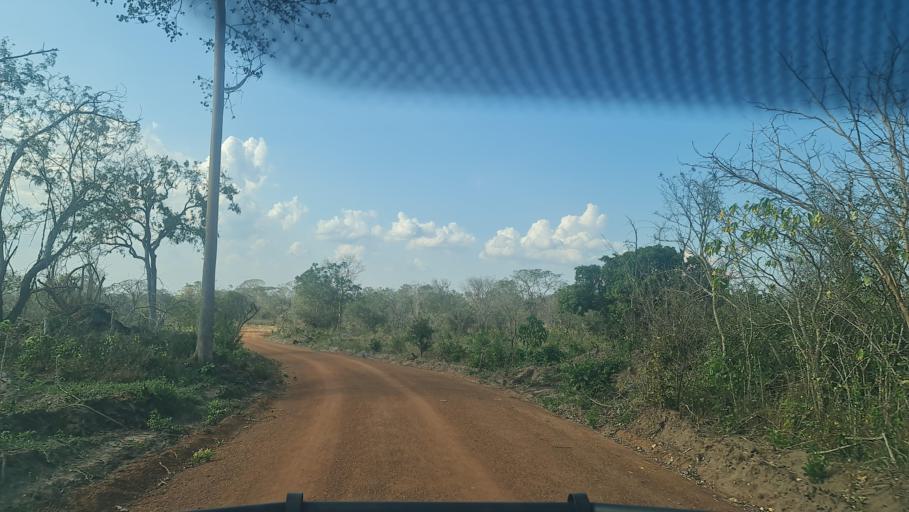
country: MZ
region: Nampula
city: Ilha de Mocambique
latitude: -15.5075
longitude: 40.1639
